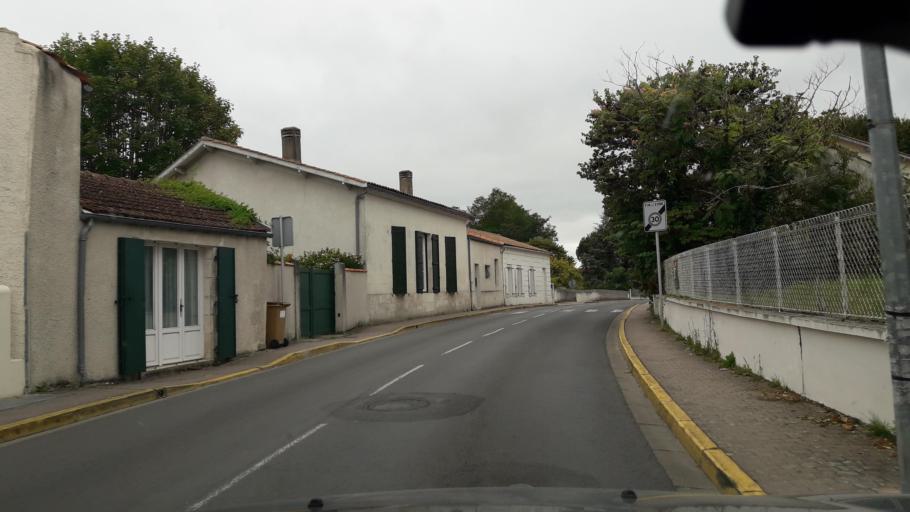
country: FR
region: Poitou-Charentes
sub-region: Departement de la Charente-Maritime
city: Les Mathes
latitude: 45.7166
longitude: -1.1480
